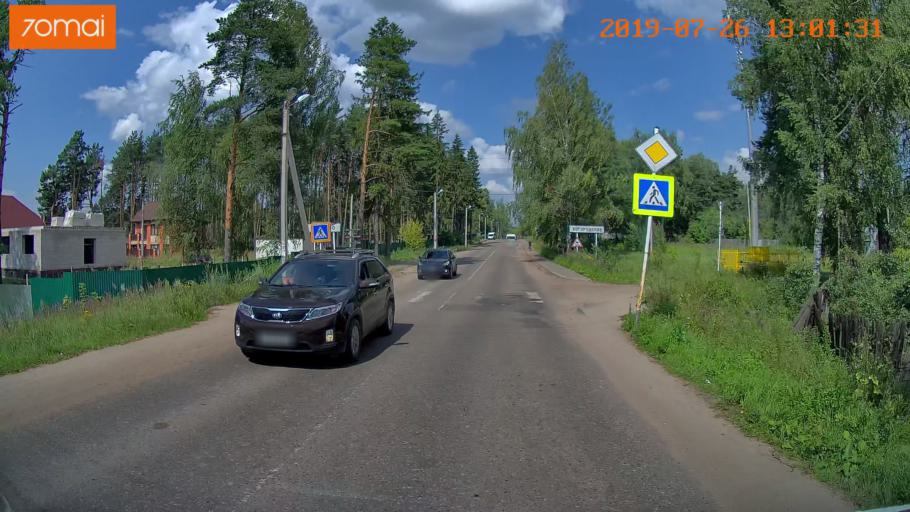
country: RU
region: Ivanovo
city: Bogorodskoye
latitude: 57.0388
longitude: 41.0126
